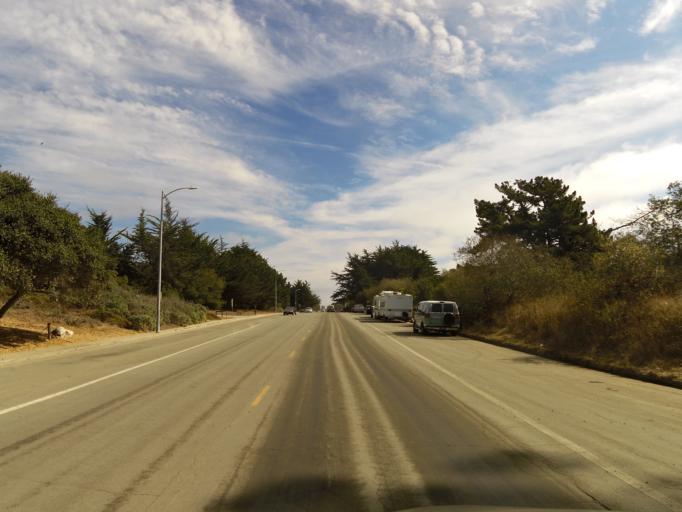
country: US
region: California
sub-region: Santa Cruz County
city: Santa Cruz
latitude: 36.9545
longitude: -122.0595
